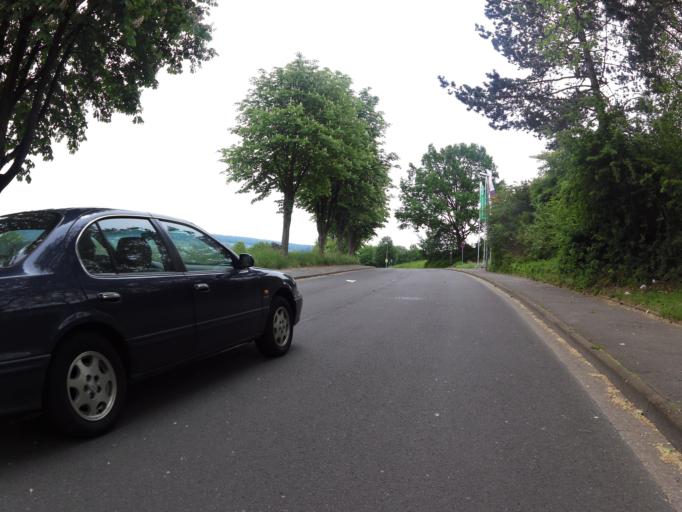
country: DE
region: North Rhine-Westphalia
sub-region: Regierungsbezirk Detmold
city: Hoexter
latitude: 51.7793
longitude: 9.3697
